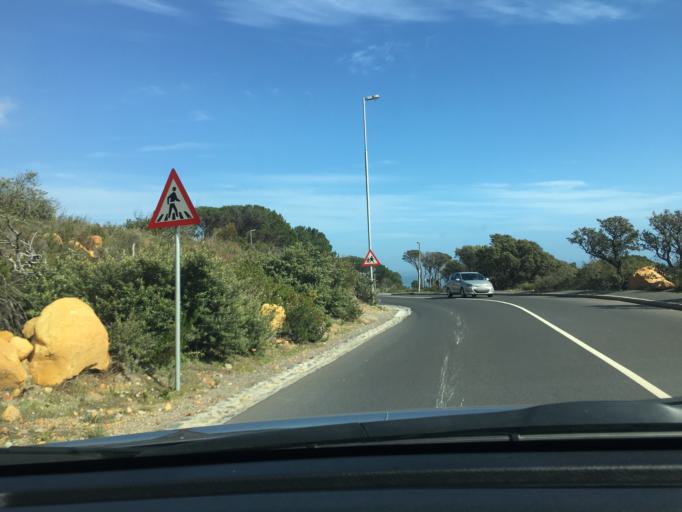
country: ZA
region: Western Cape
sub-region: City of Cape Town
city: Cape Town
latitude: -33.9581
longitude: 18.3840
